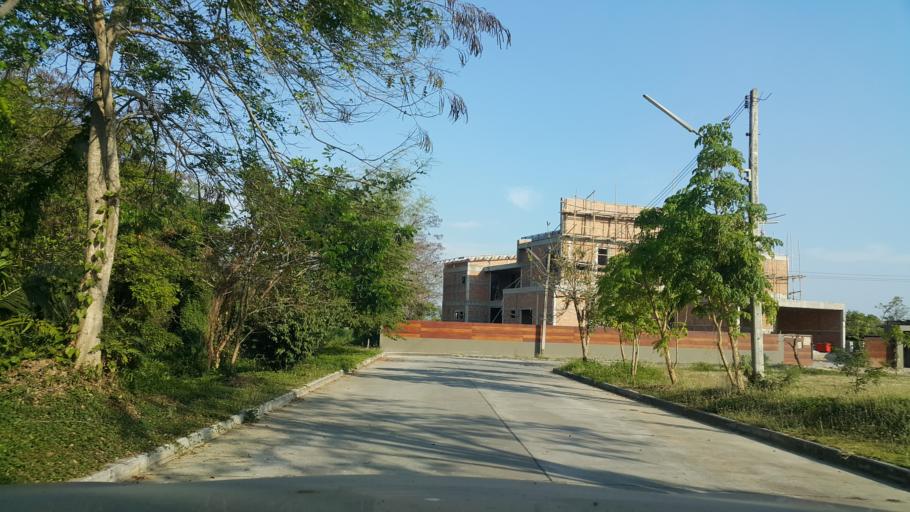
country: TH
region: Chiang Mai
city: San Sai
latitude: 18.8402
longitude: 99.0971
